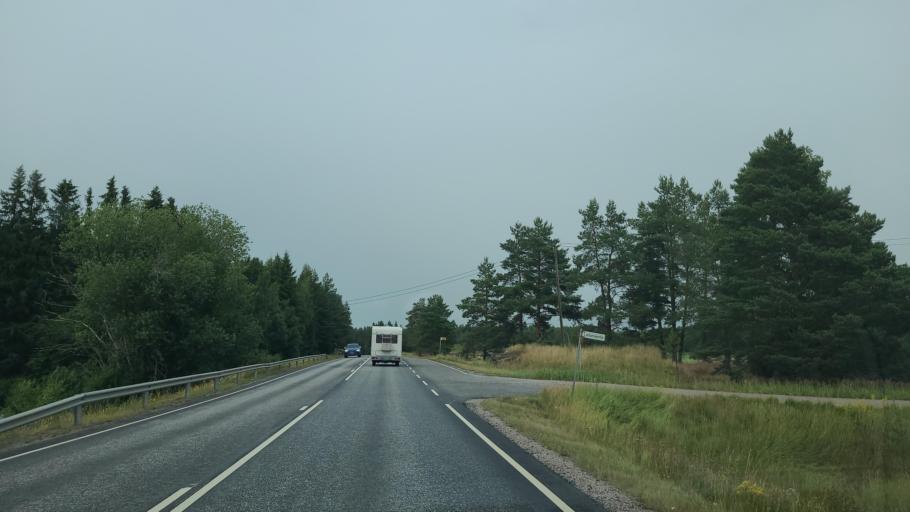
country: FI
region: Varsinais-Suomi
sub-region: Turku
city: Sauvo
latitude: 60.2951
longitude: 22.6761
